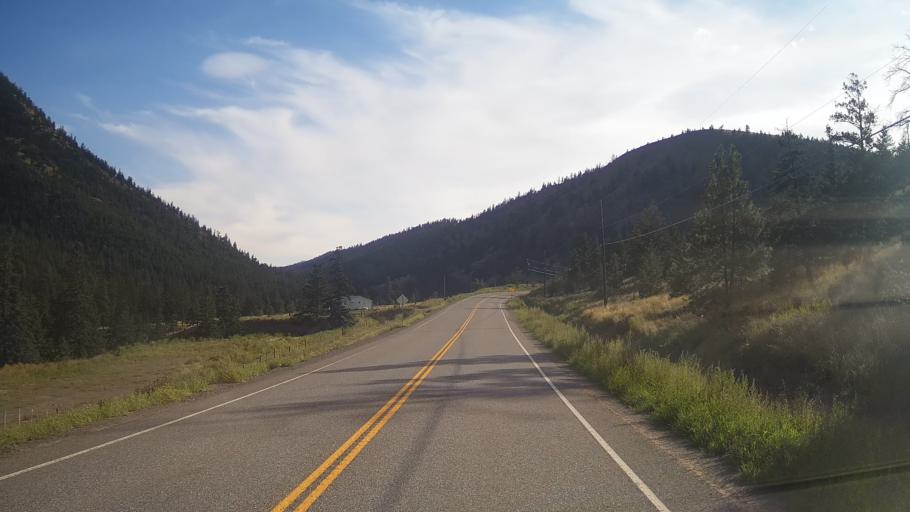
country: CA
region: British Columbia
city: Cache Creek
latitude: 50.8786
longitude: -121.5114
